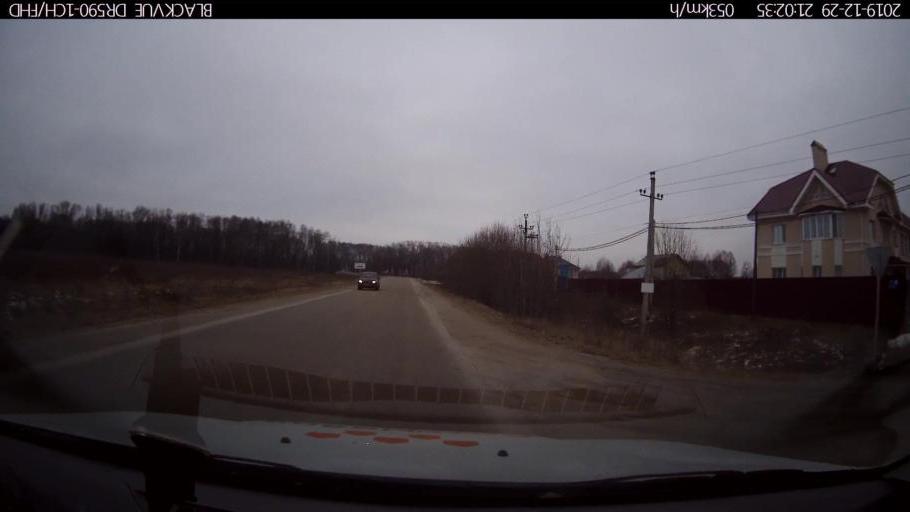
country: RU
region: Nizjnij Novgorod
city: Afonino
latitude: 56.1908
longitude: 44.0014
